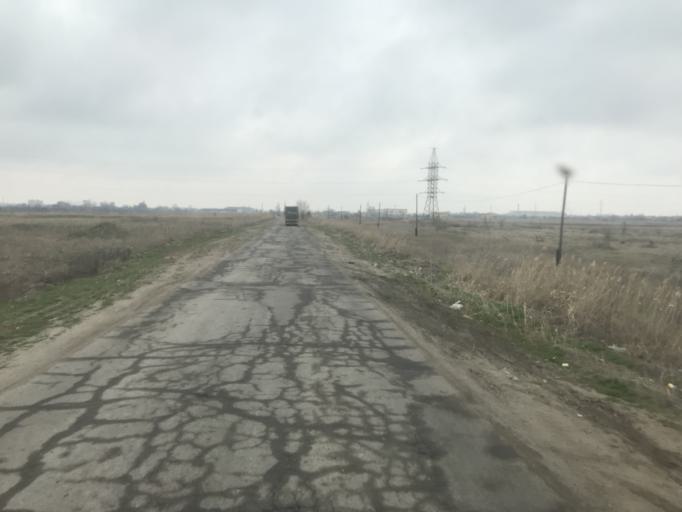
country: RU
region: Volgograd
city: Svetlyy Yar
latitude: 48.5172
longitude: 44.6289
